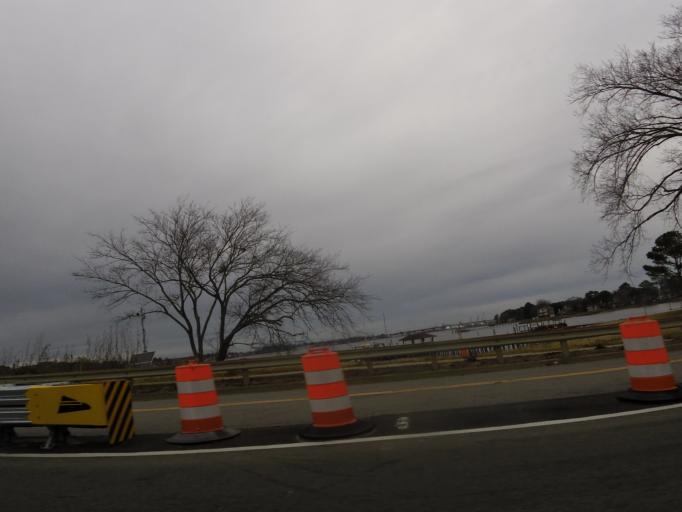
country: US
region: Virginia
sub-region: City of Portsmouth
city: Portsmouth Heights
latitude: 36.8416
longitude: -76.3589
